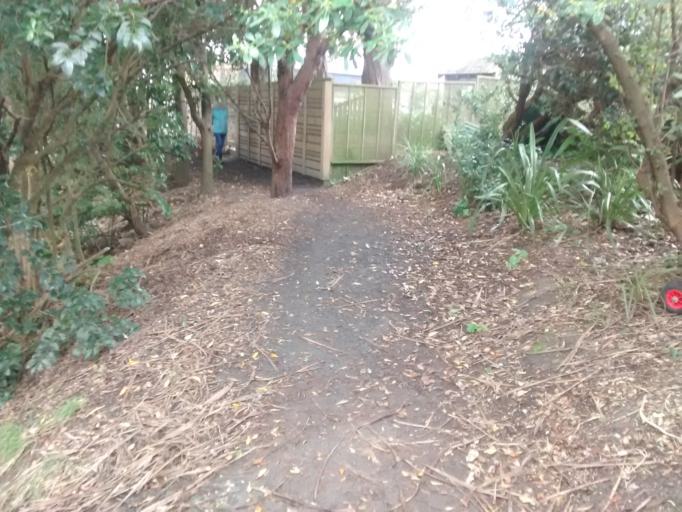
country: NZ
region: Auckland
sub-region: Auckland
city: Rosebank
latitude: -36.8560
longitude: 174.7124
